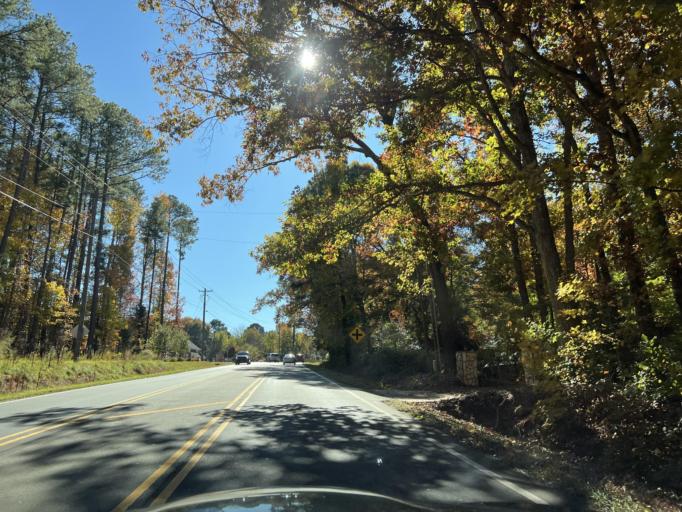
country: US
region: North Carolina
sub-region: Wake County
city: Garner
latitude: 35.7163
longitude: -78.6858
